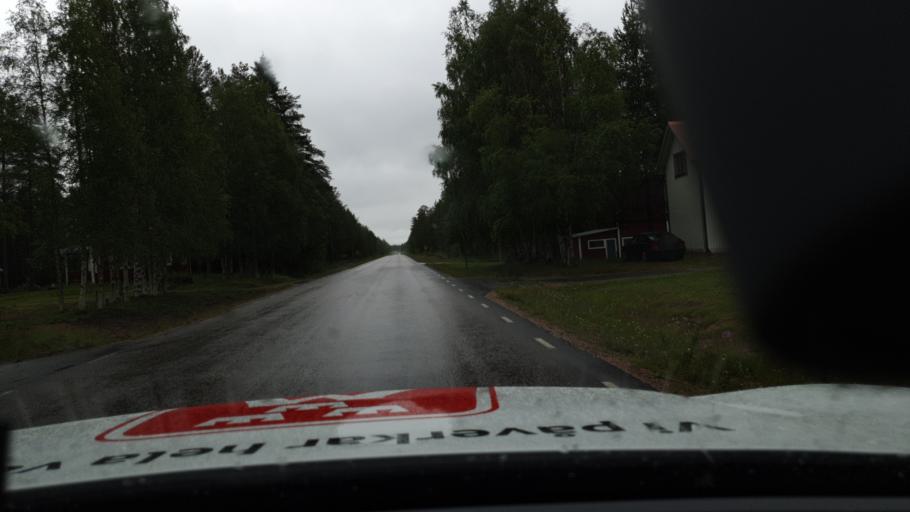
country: SE
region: Norrbotten
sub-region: Overtornea Kommun
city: OEvertornea
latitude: 66.4716
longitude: 23.6733
